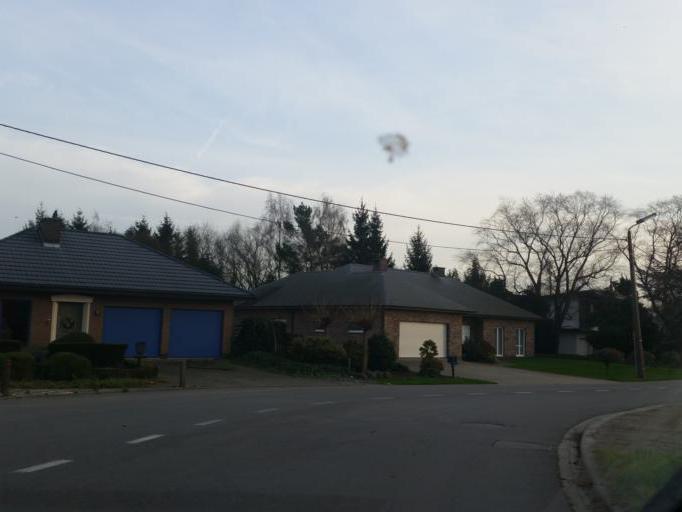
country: BE
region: Flanders
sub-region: Provincie Antwerpen
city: Sint-Katelijne-Waver
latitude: 51.0657
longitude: 4.5188
